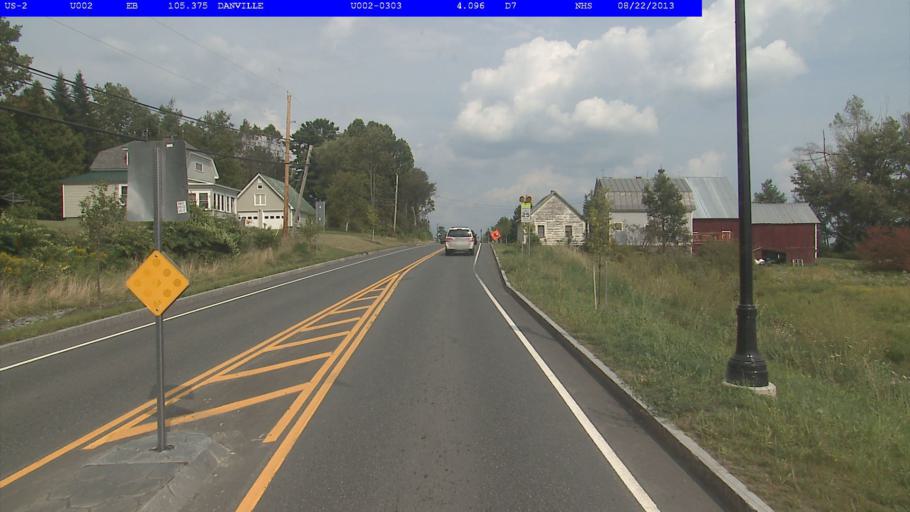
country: US
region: Vermont
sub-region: Caledonia County
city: Saint Johnsbury
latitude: 44.4111
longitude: -72.1474
